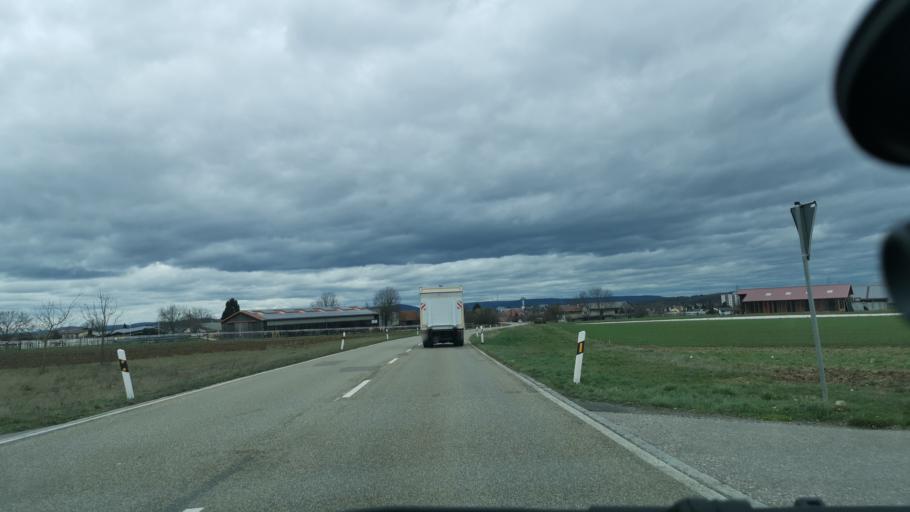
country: DE
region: Baden-Wuerttemberg
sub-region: Regierungsbezirk Stuttgart
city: Markgroningen
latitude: 48.8911
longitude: 9.0901
